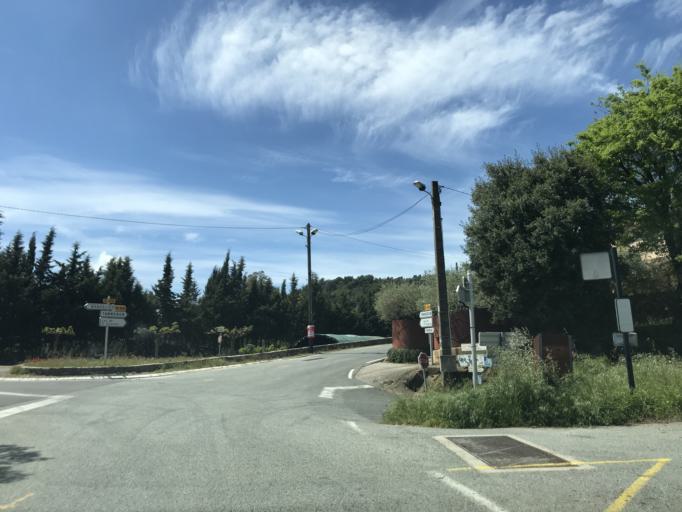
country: FR
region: Provence-Alpes-Cote d'Azur
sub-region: Departement du Var
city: Tanneron
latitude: 43.5849
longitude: 6.8871
